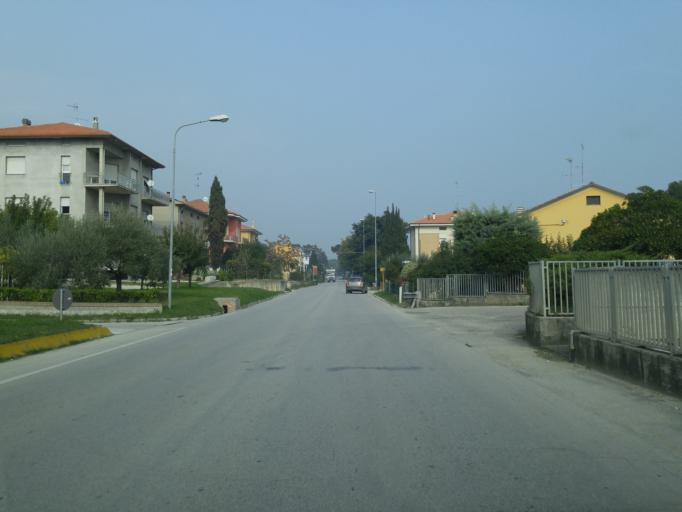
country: IT
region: The Marches
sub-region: Provincia di Pesaro e Urbino
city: Calcinelli
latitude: 43.7604
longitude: 12.9261
